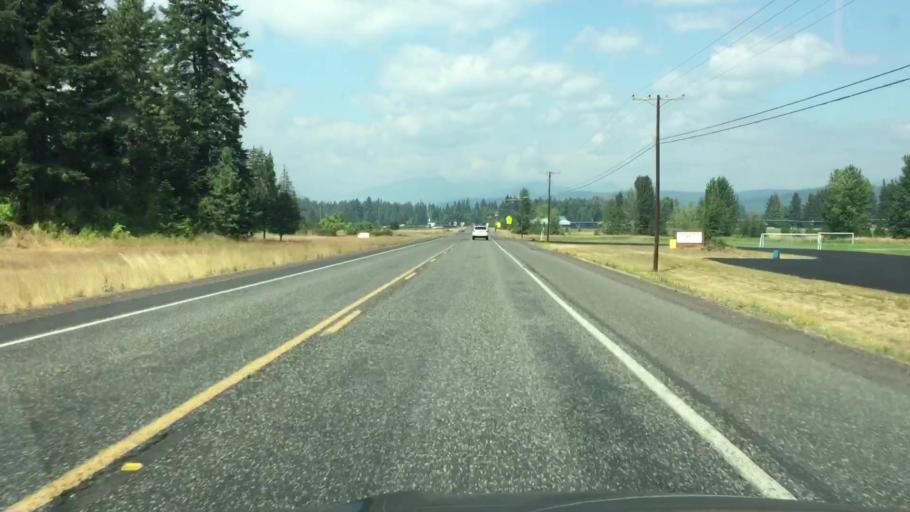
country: US
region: Washington
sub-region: Klickitat County
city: White Salmon
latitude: 45.9885
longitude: -121.5167
